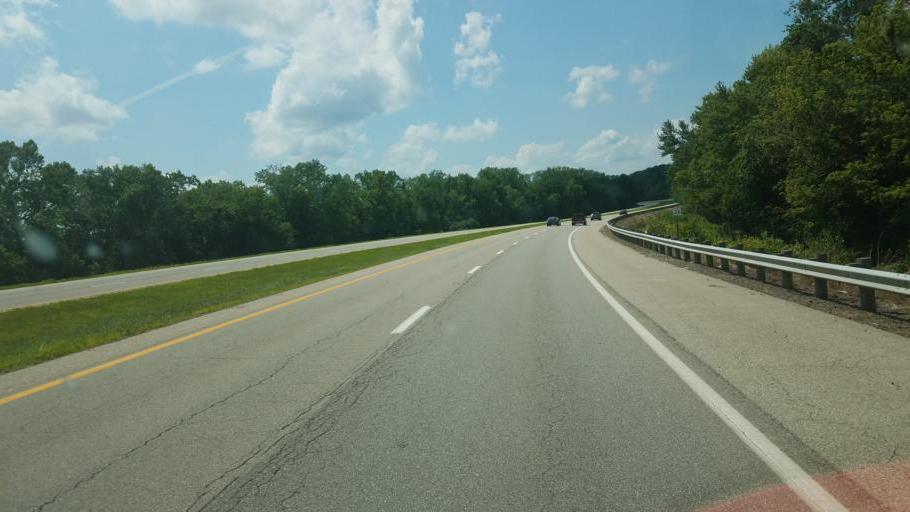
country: US
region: Ohio
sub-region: Coshocton County
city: West Lafayette
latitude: 40.2910
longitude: -81.7931
